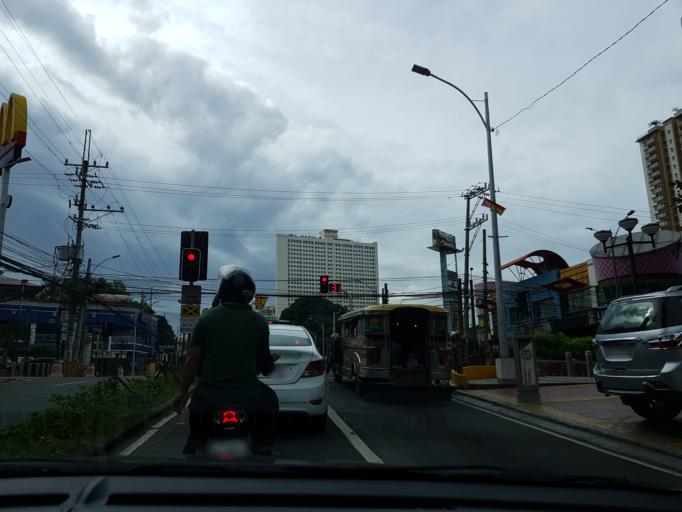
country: PH
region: Calabarzon
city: Del Monte
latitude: 14.6290
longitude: 121.0340
